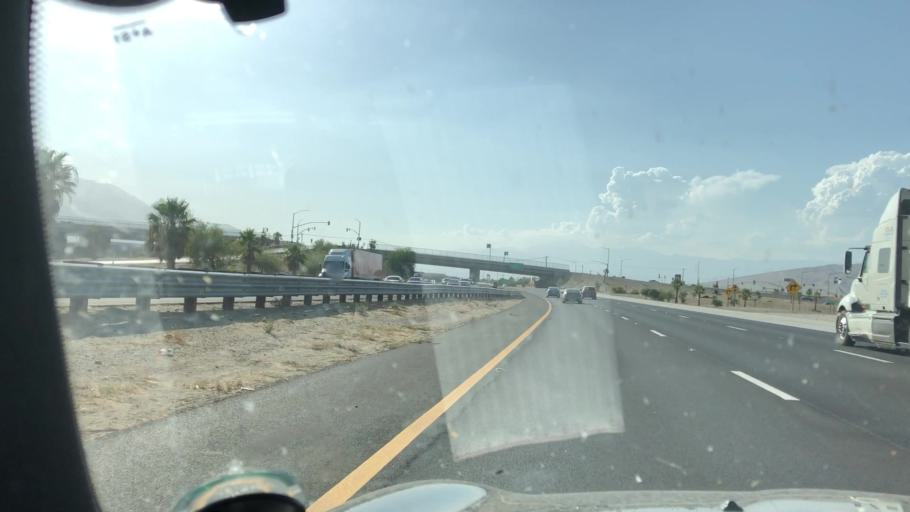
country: US
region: California
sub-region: Riverside County
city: Thousand Palms
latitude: 33.8048
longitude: -116.3851
